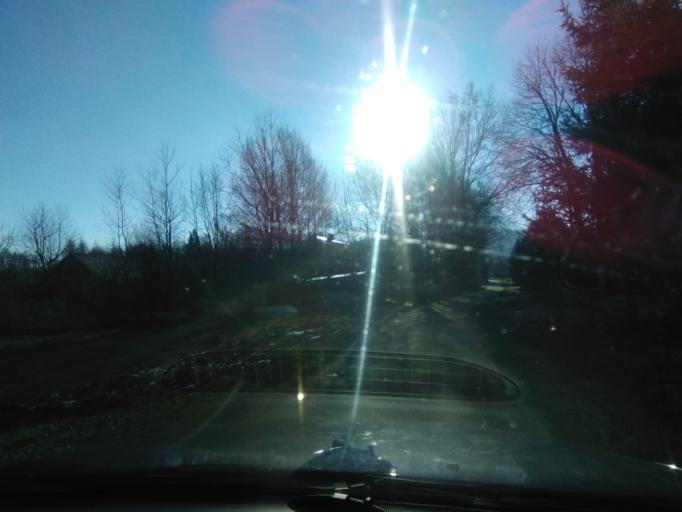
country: PL
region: Subcarpathian Voivodeship
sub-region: Powiat krosnienski
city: Rymanow
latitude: 49.5613
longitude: 21.8916
